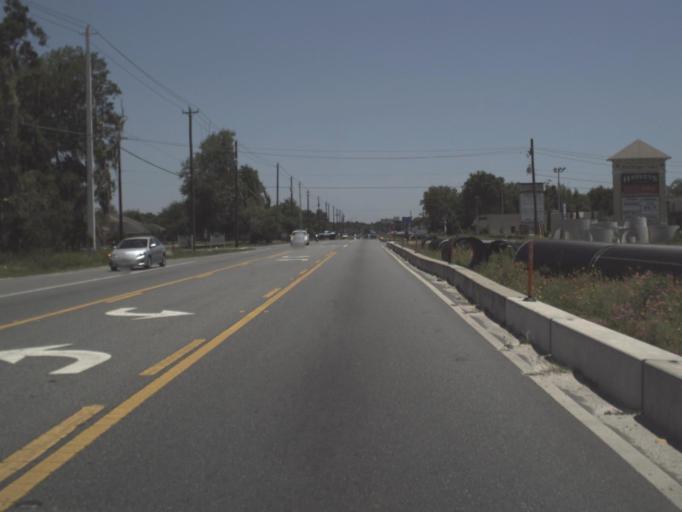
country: US
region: Florida
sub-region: Columbia County
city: Lake City
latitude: 30.1842
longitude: -82.7086
